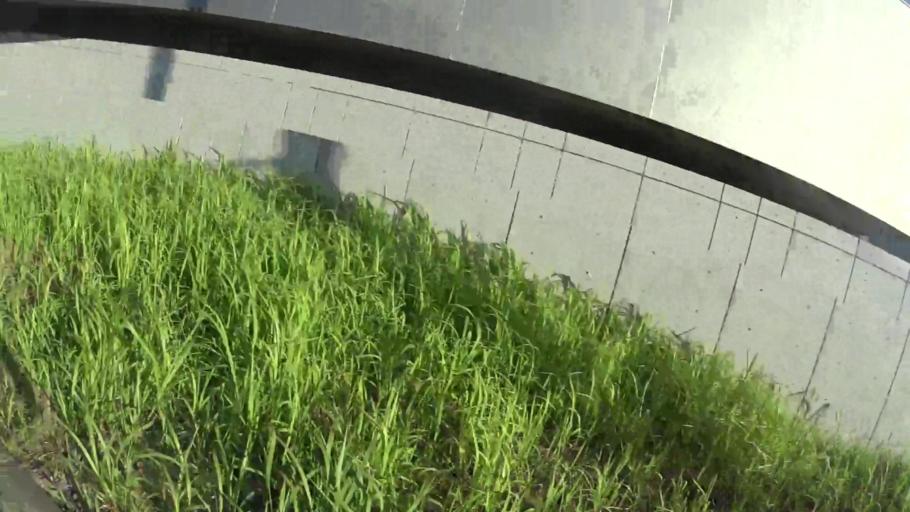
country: JP
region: Chiba
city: Oami
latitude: 35.5218
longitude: 140.2812
